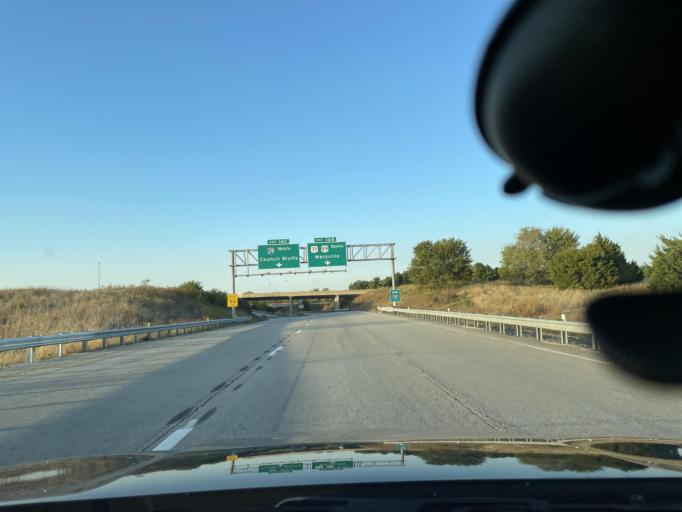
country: US
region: Missouri
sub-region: Andrew County
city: Country Club Village
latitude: 39.8827
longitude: -94.8568
